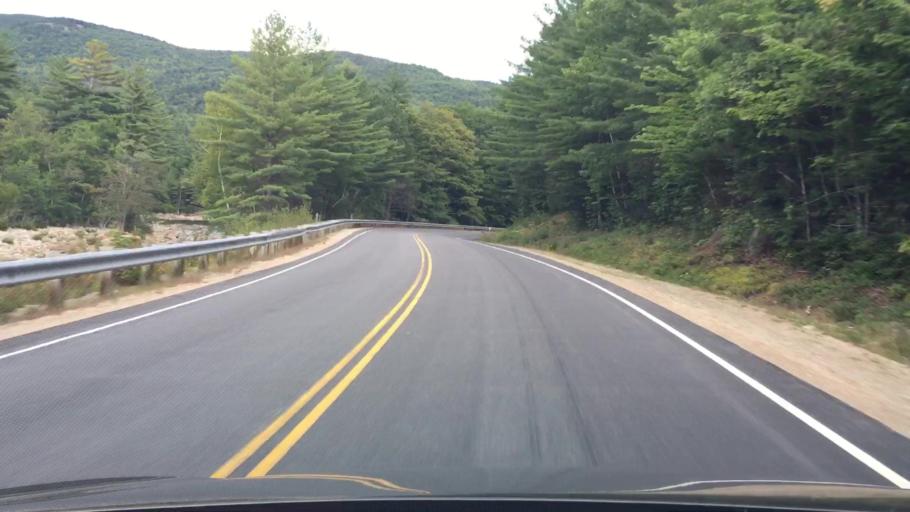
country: US
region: New Hampshire
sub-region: Carroll County
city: Conway
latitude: 44.0008
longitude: -71.2343
